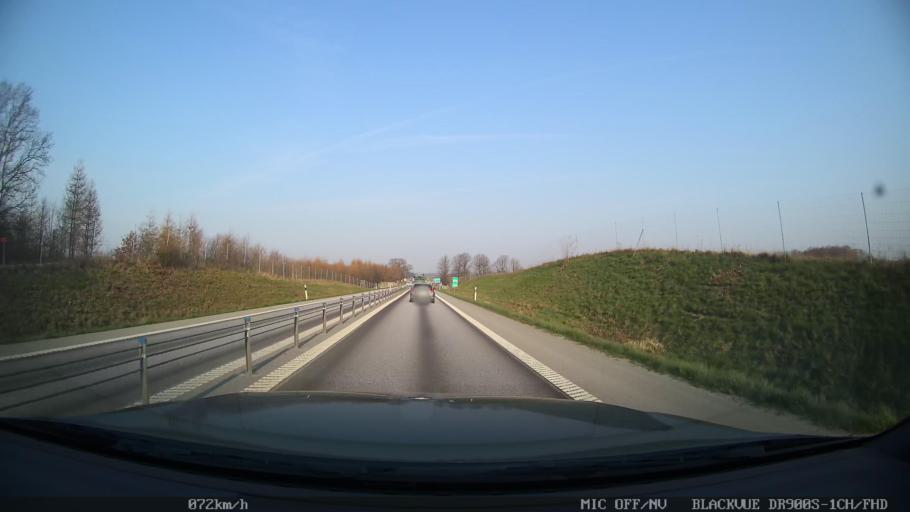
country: SE
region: Skane
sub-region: Svedala Kommun
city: Svedala
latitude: 55.5129
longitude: 13.3057
